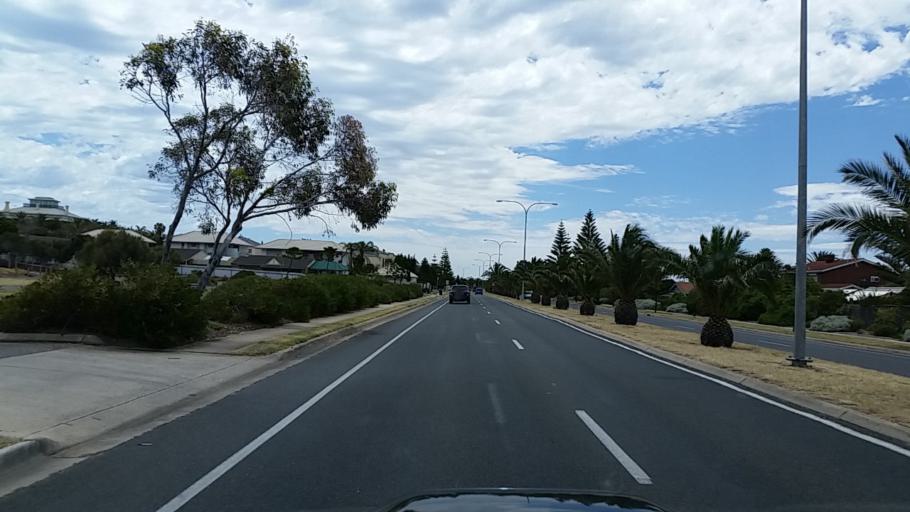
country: AU
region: South Australia
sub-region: Charles Sturt
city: West Lakes Shore
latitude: -34.8803
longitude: 138.4852
